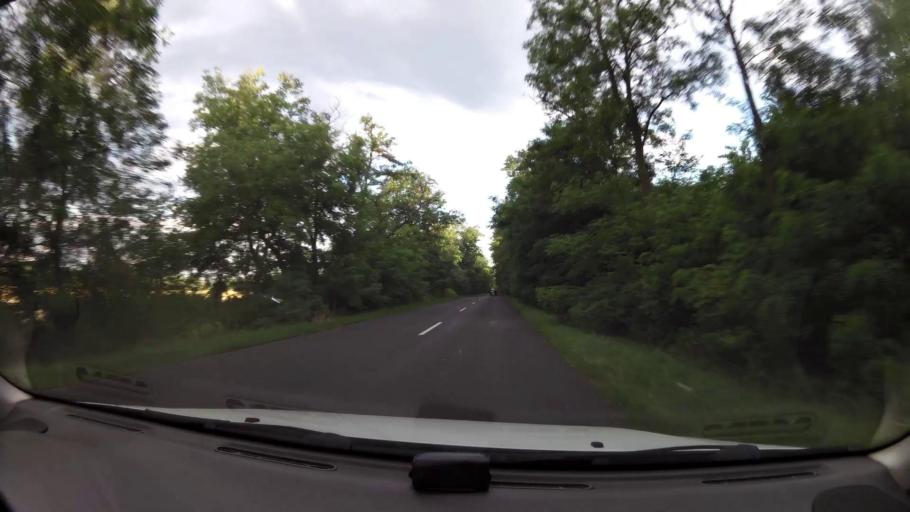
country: HU
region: Pest
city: Tapioszecso
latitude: 47.4253
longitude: 19.6068
